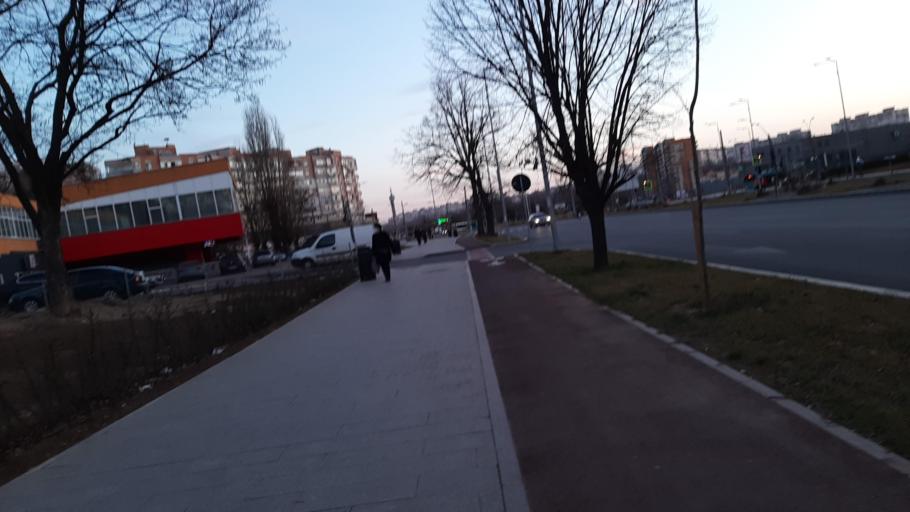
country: RO
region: Galati
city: Galati
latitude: 45.4288
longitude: 28.0248
